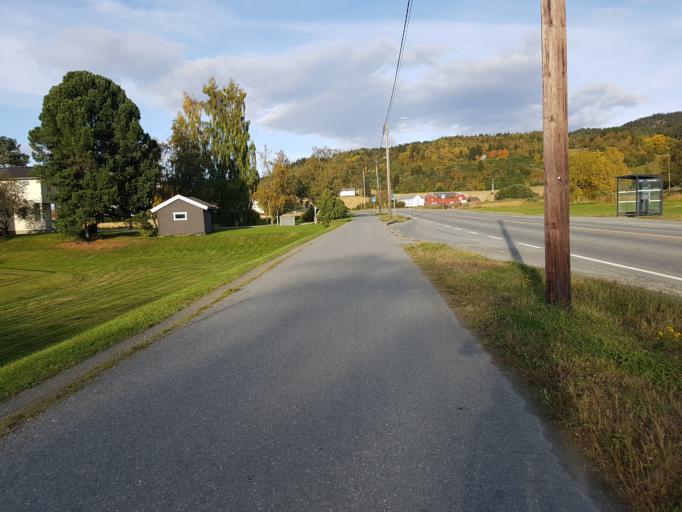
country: NO
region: Sor-Trondelag
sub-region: Trondheim
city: Trondheim
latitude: 63.3770
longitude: 10.4306
